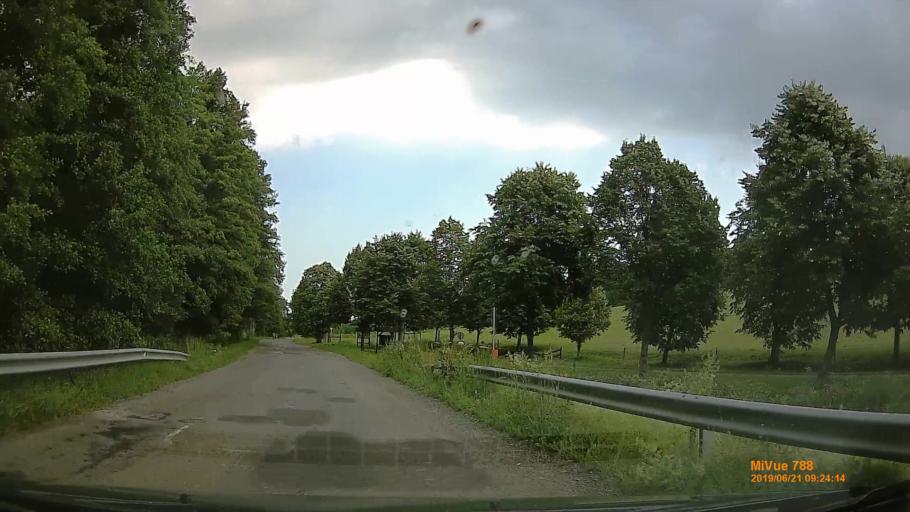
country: HU
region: Somogy
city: Taszar
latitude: 46.2541
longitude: 17.9066
